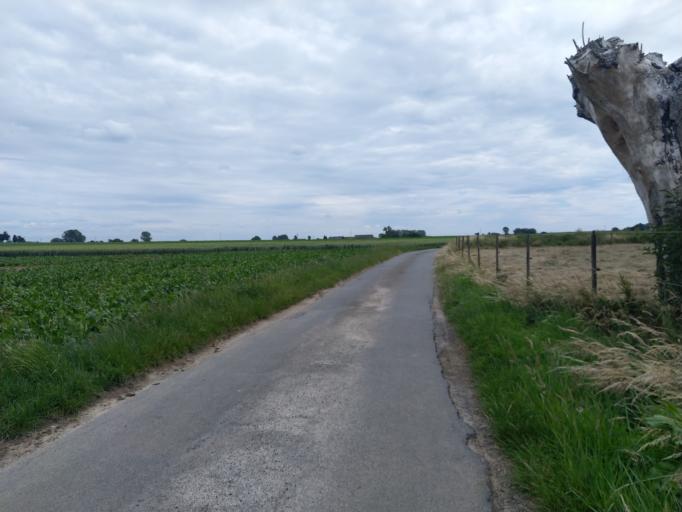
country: BE
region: Wallonia
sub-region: Province du Hainaut
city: Chievres
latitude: 50.5403
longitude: 3.8165
